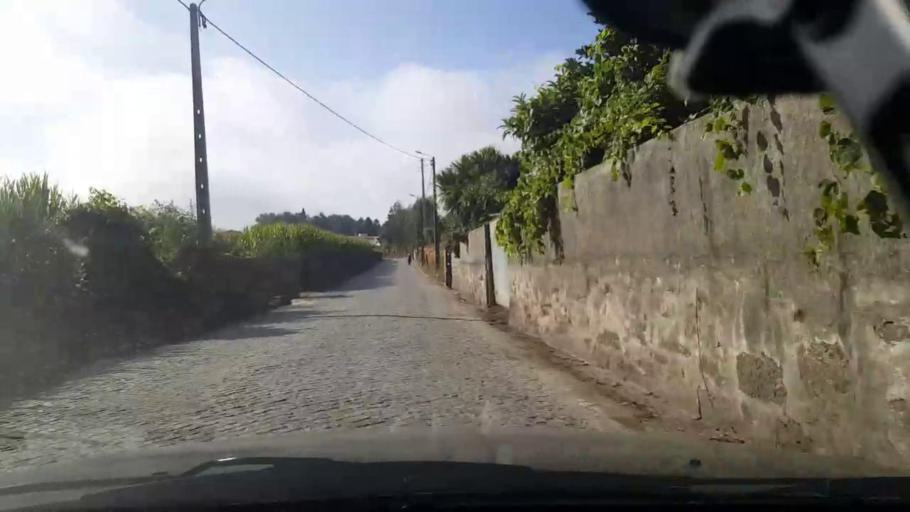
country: PT
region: Porto
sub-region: Maia
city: Gemunde
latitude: 41.2683
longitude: -8.6753
